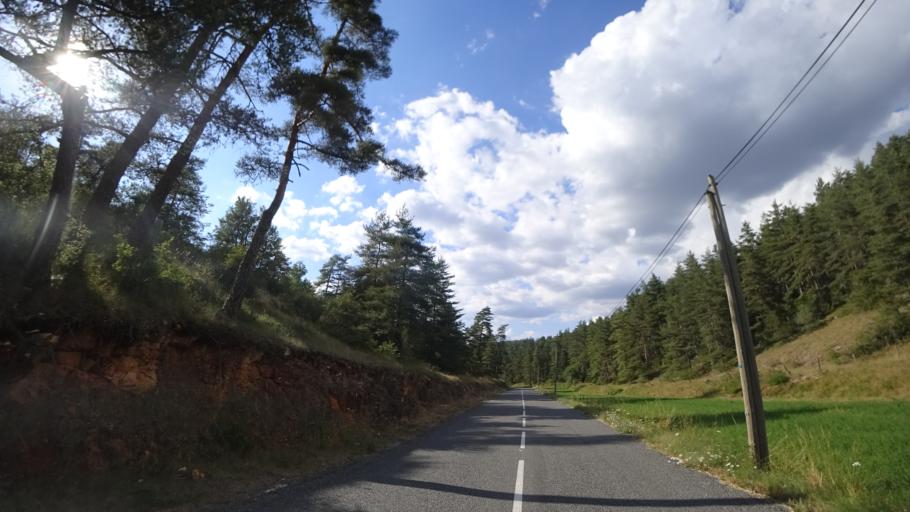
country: FR
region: Languedoc-Roussillon
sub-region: Departement de la Lozere
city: Chanac
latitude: 44.3975
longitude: 3.2964
